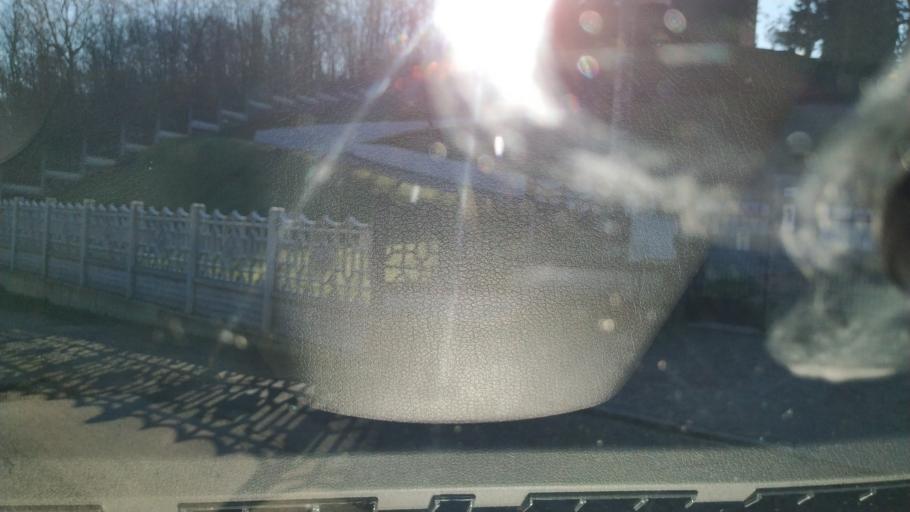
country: IT
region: Piedmont
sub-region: Provincia di Biella
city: Brusnengo
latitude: 45.5903
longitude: 8.2645
